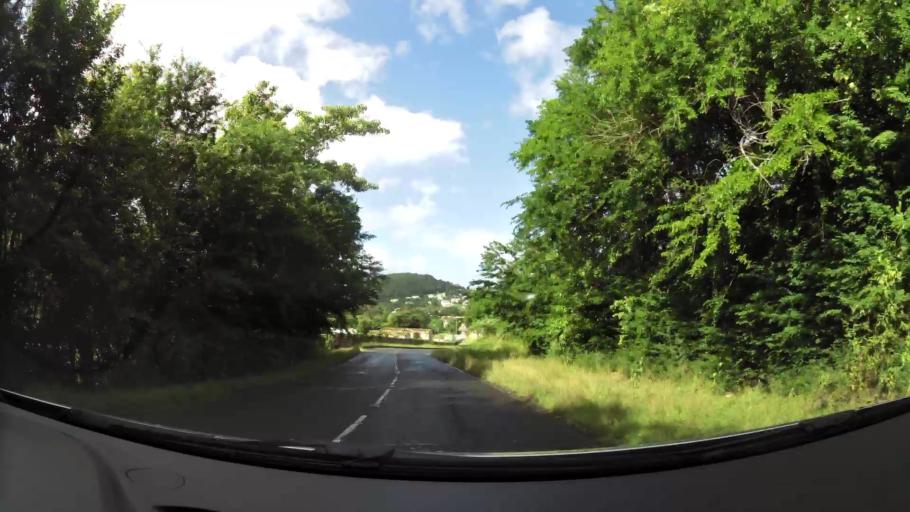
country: MQ
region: Martinique
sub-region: Martinique
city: Les Trois-Ilets
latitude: 14.5384
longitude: -61.0582
